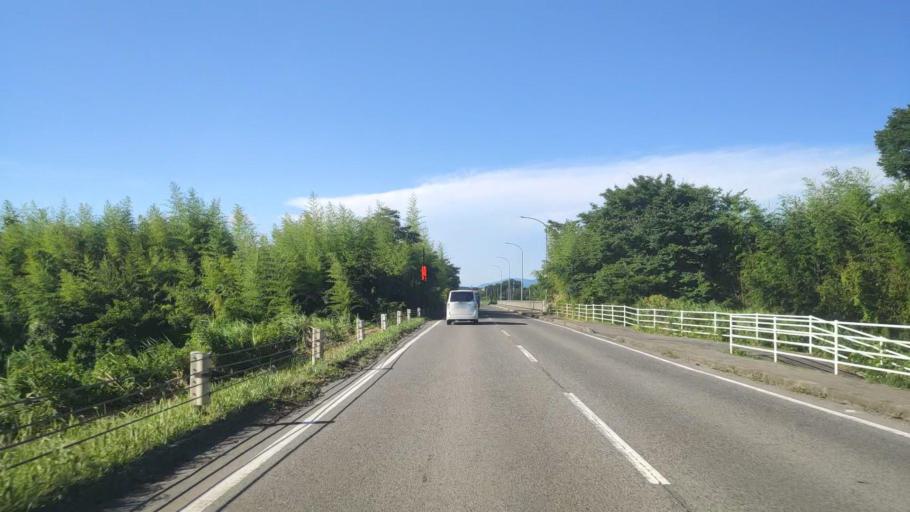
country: JP
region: Shiga Prefecture
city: Hino
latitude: 35.0044
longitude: 136.2384
